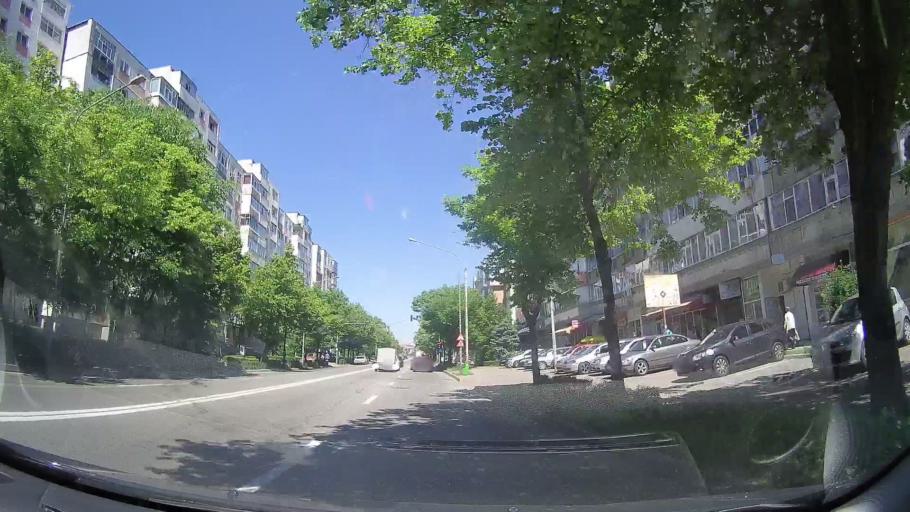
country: RO
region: Arges
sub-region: Comuna Bradu
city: Geamana
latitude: 44.8362
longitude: 24.9025
